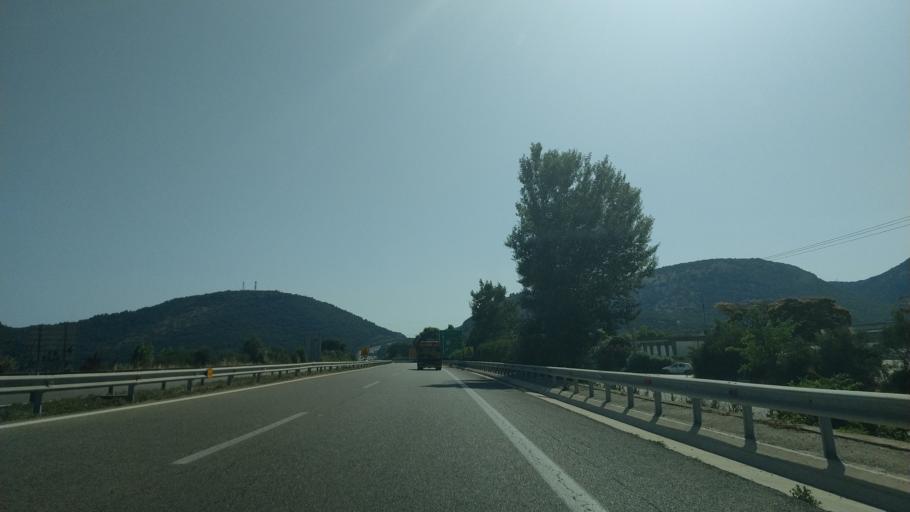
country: GR
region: East Macedonia and Thrace
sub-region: Nomos Kavalas
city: Nea Karvali
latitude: 40.9623
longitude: 24.4776
